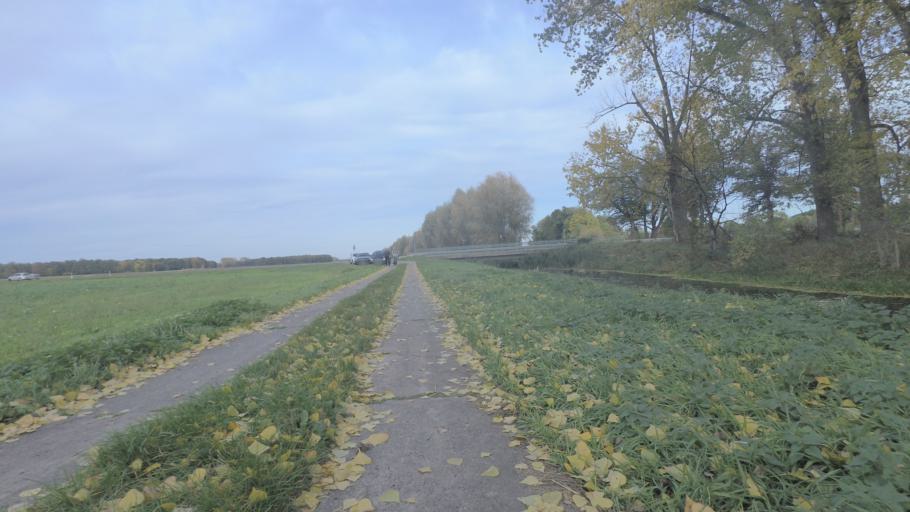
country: DE
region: Brandenburg
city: Ludwigsfelde
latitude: 52.2720
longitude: 13.3028
